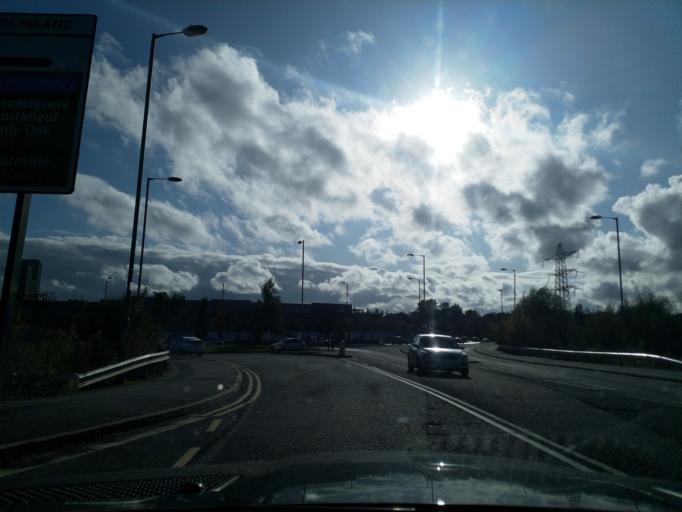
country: GB
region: England
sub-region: City and Borough of Birmingham
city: Birmingham
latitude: 52.4476
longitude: -1.9389
